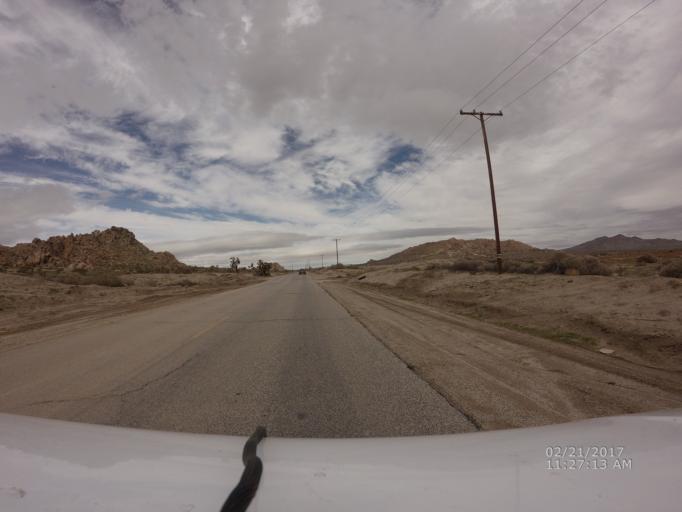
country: US
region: California
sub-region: Los Angeles County
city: Lake Los Angeles
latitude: 34.6392
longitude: -117.8629
